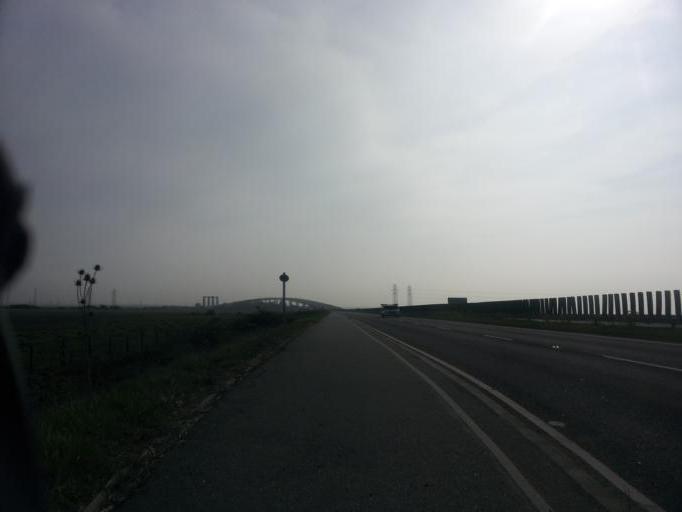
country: GB
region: England
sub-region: Kent
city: Queenborough
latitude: 51.3991
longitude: 0.7630
